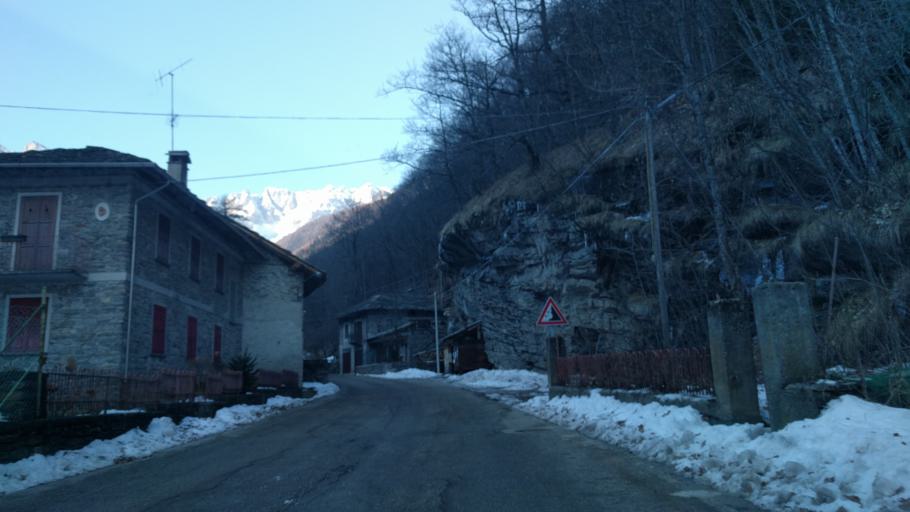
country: IT
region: Piedmont
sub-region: Provincia di Torino
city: Groscavallo
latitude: 45.3678
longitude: 7.2560
